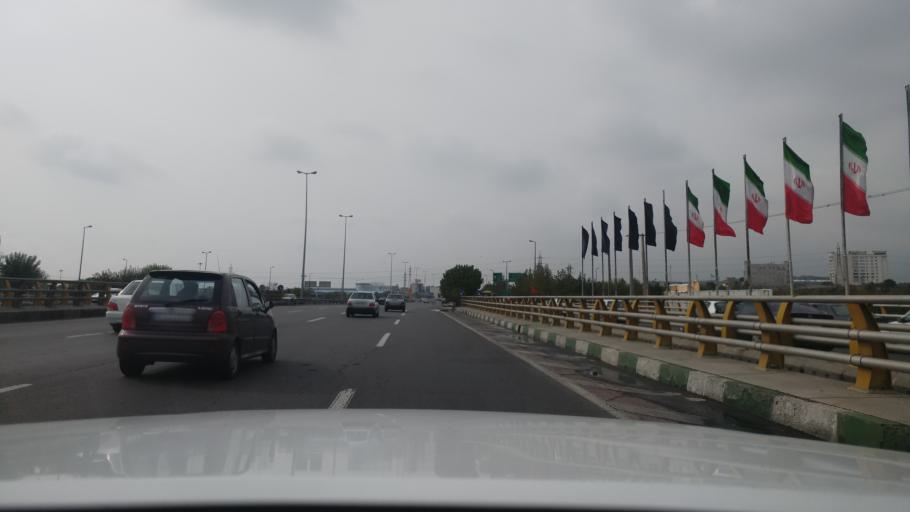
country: IR
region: Tehran
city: Shahr-e Qods
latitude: 35.7146
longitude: 51.2526
